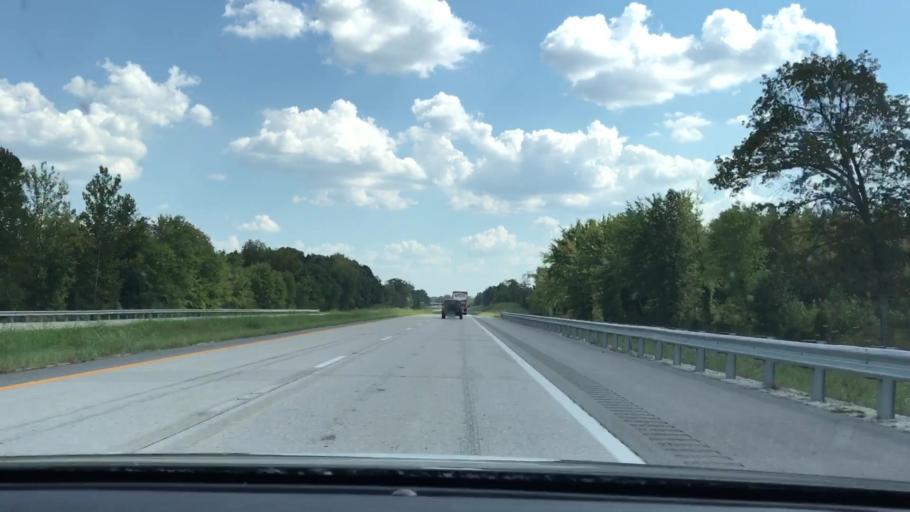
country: US
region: Kentucky
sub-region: Ohio County
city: Oak Grove
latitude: 37.3642
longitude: -86.7963
